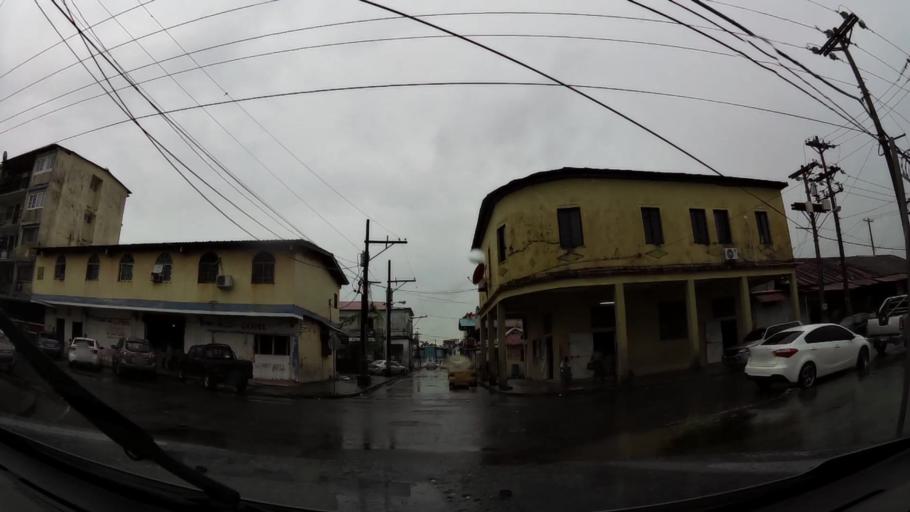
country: PA
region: Colon
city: Colon
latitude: 9.3650
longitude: -79.9021
